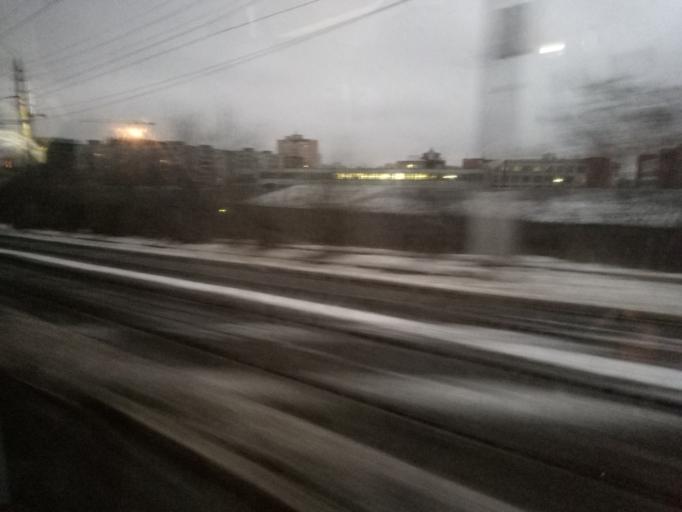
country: RU
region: Tula
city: Tula
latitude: 54.2039
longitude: 37.5850
